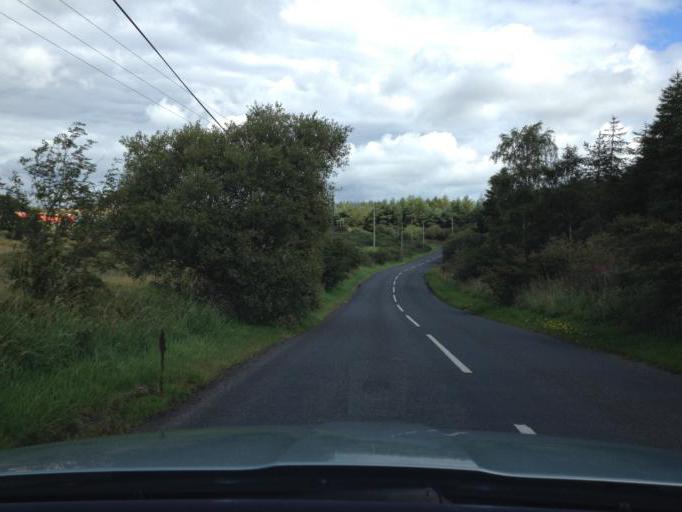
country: GB
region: Scotland
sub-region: Falkirk
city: Polmont
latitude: 55.9428
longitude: -3.7496
